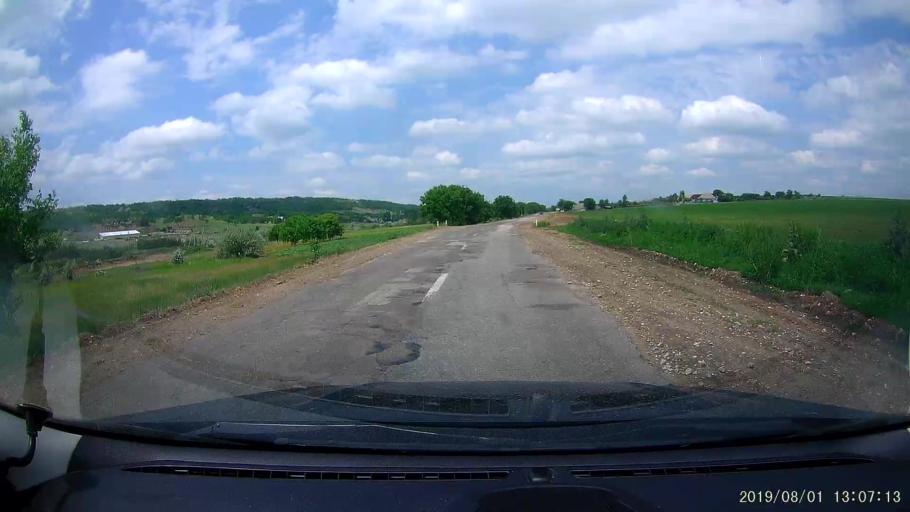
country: MD
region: Gagauzia
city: Vulcanesti
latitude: 45.8082
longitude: 28.3445
